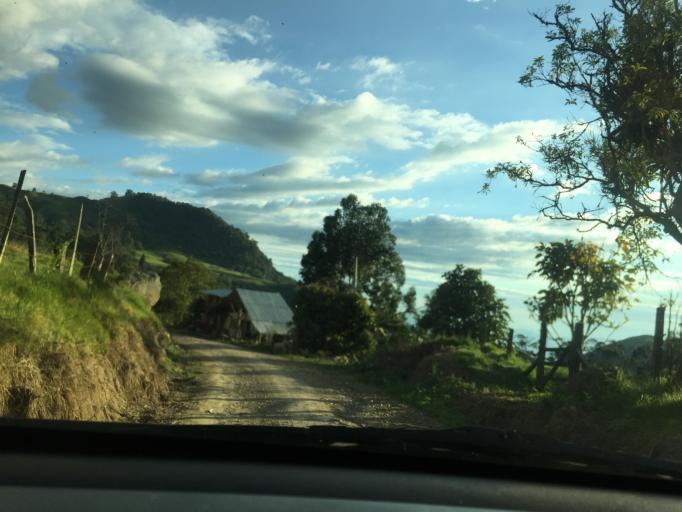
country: CO
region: Cundinamarca
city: Zipacon
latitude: 4.7246
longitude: -74.3892
